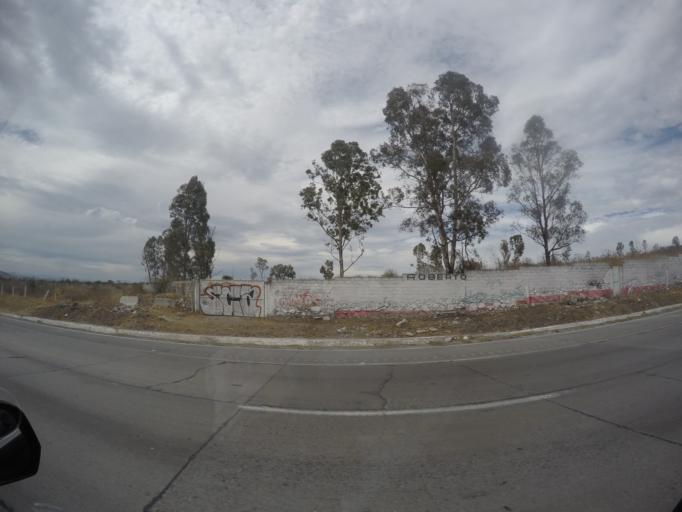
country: MX
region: Queretaro
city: San Juan del Rio
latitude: 20.3627
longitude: -99.9709
